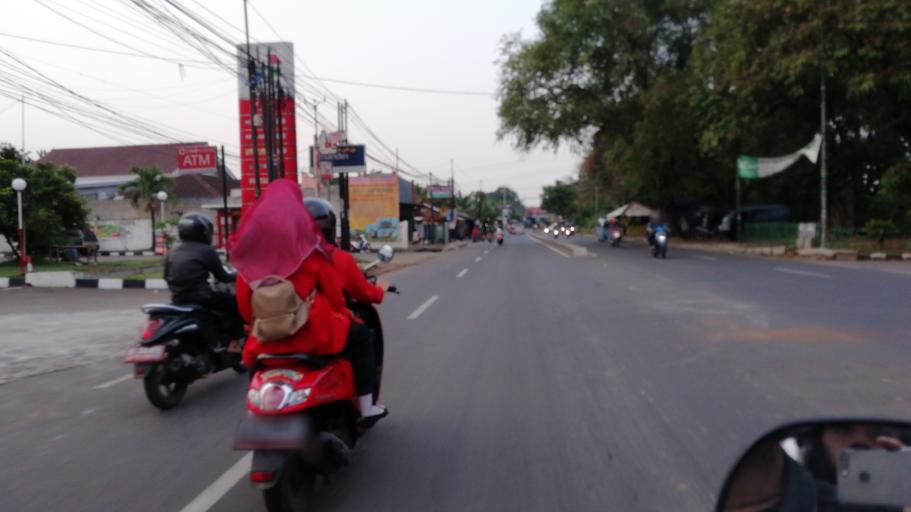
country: ID
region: West Java
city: Depok
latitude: -6.4234
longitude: 106.8569
